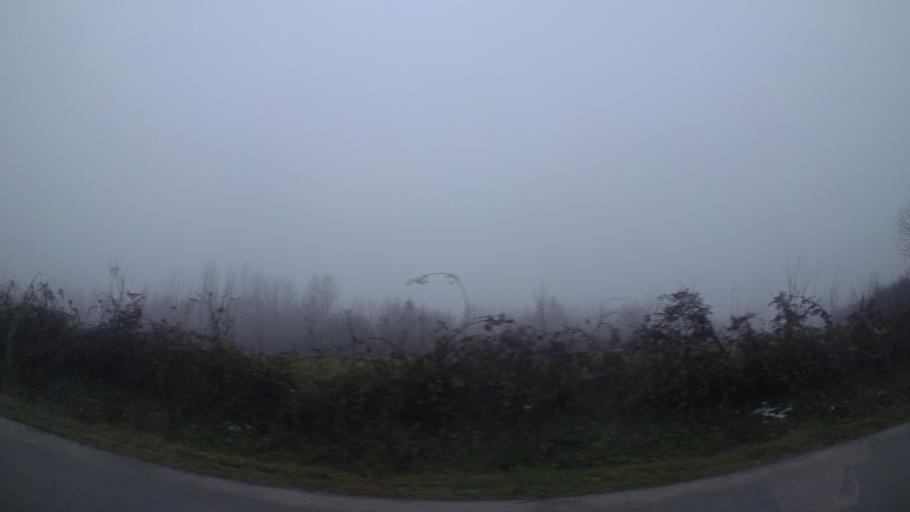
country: HR
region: Sisacko-Moslavacka
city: Glina
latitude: 45.3270
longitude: 16.0386
